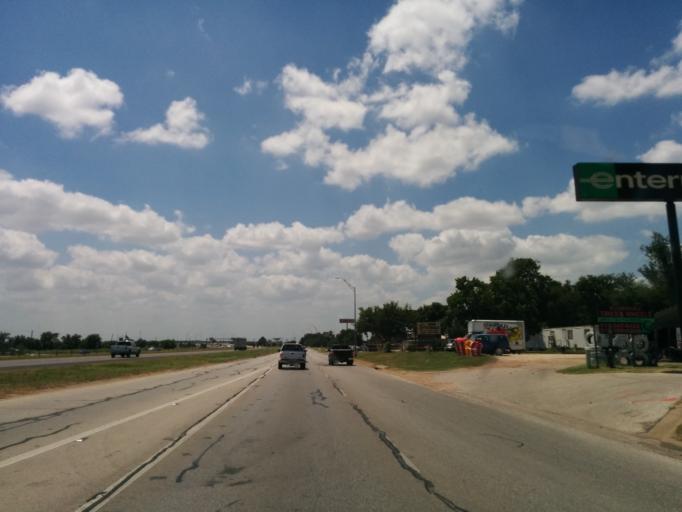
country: US
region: Texas
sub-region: Bastrop County
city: Bastrop
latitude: 30.1093
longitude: -97.3397
